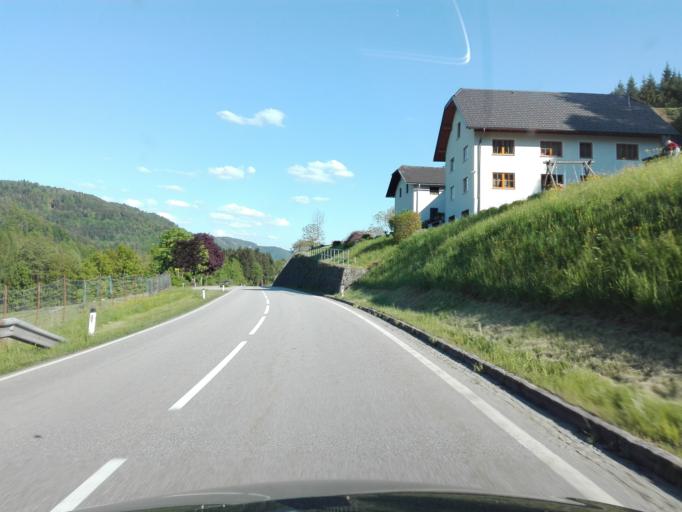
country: AT
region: Upper Austria
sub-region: Politischer Bezirk Rohrbach
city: Pfarrkirchen im Muehlkreis
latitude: 48.4784
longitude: 13.7622
